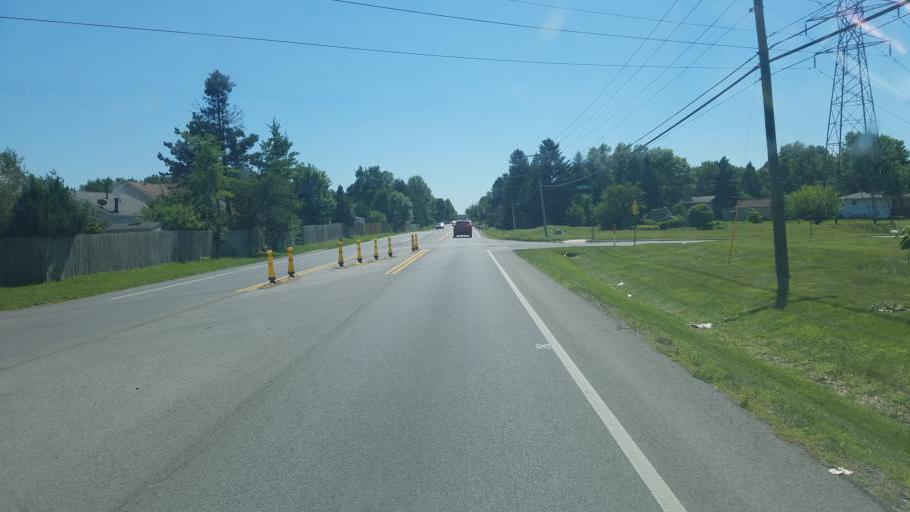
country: US
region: Ohio
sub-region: Franklin County
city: Huber Ridge
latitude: 40.0676
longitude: -82.9101
